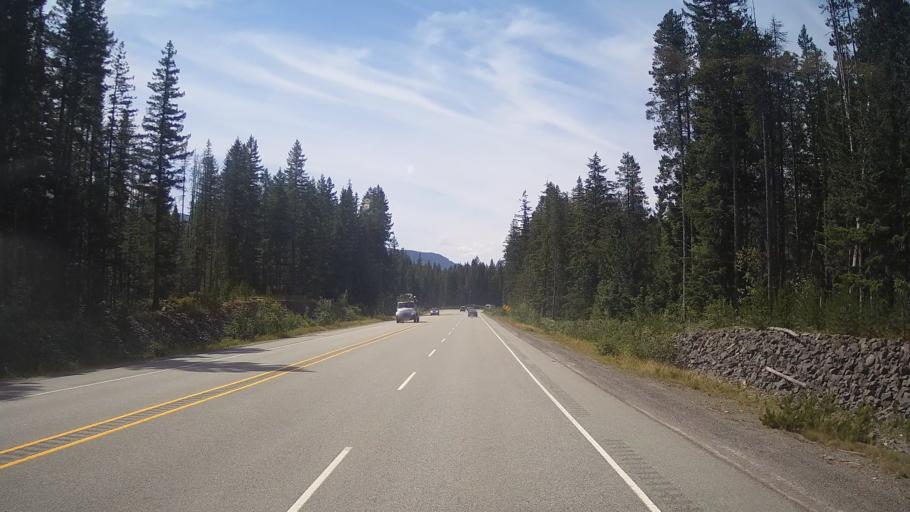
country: CA
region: British Columbia
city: Whistler
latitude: 49.9941
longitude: -123.1369
